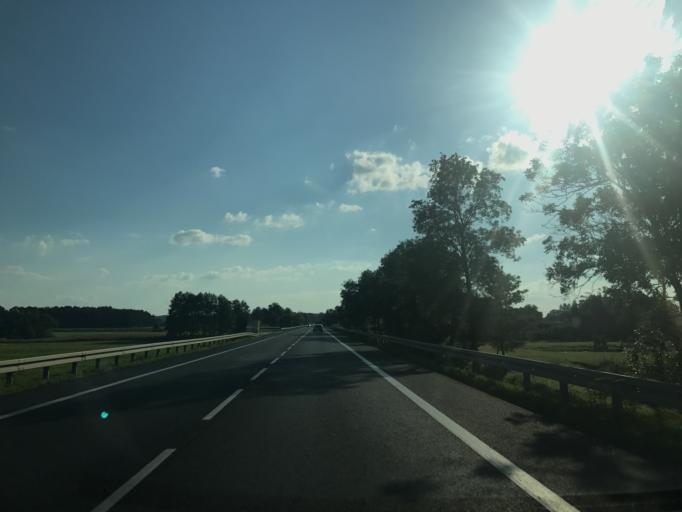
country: PL
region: Greater Poland Voivodeship
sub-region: Powiat kolski
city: Koscielec
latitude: 52.1804
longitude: 18.5976
